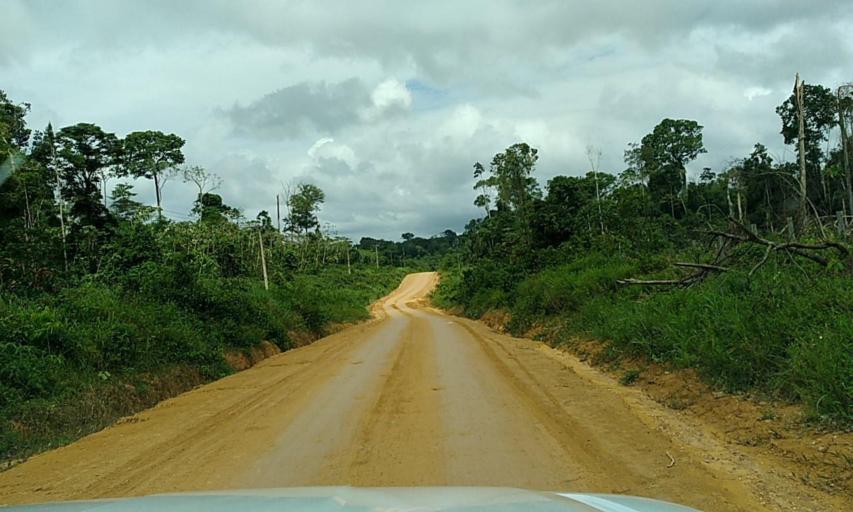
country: BR
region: Para
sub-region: Senador Jose Porfirio
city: Senador Jose Porfirio
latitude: -2.7593
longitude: -51.7911
